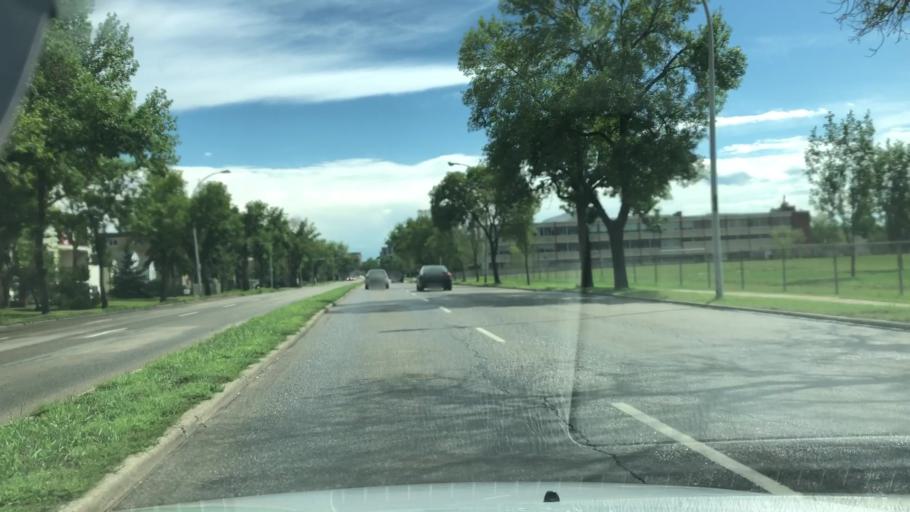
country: CA
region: Alberta
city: Edmonton
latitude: 53.5562
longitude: -113.5085
